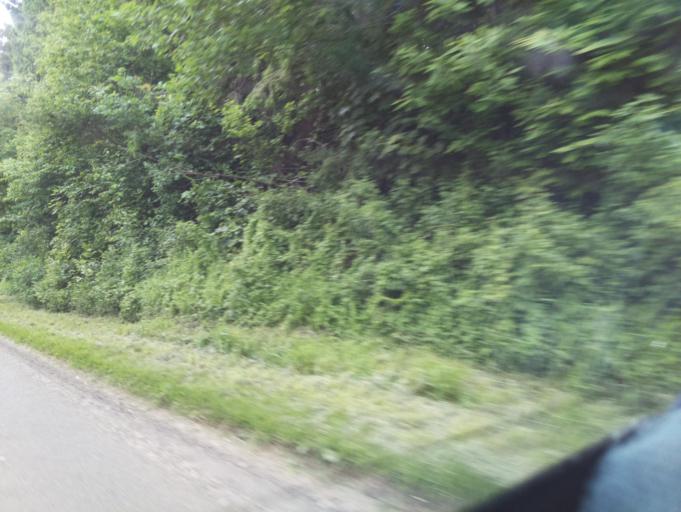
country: GB
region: England
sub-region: Herefordshire
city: Yatton
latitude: 51.9525
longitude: -2.5271
